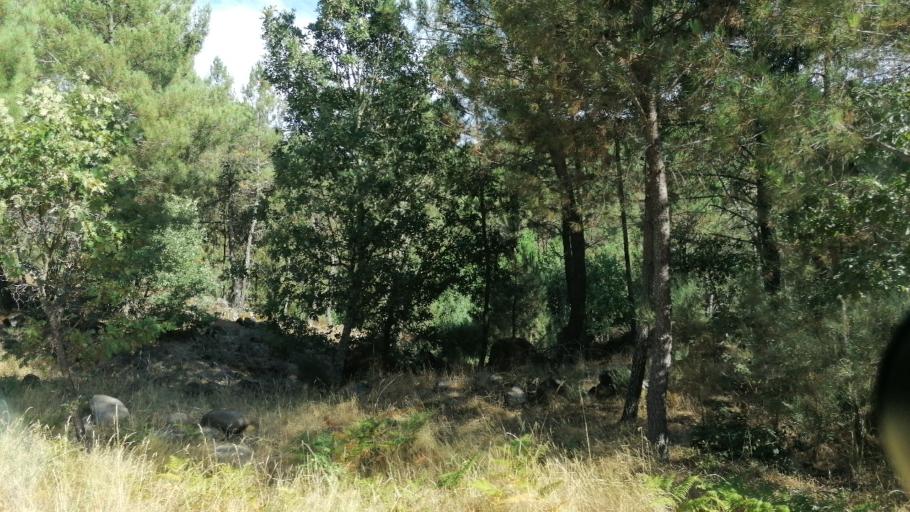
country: PT
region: Vila Real
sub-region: Sabrosa
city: Sabrosa
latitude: 41.3566
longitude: -7.5797
